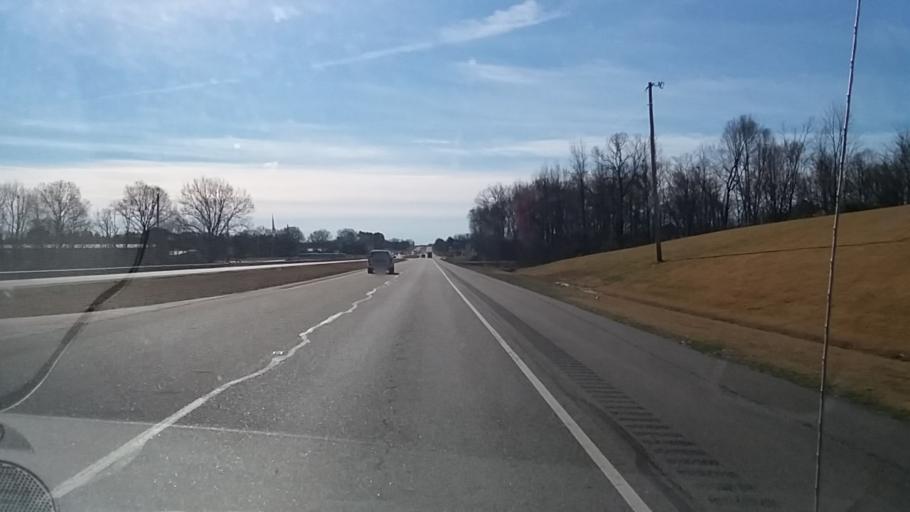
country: US
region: Tennessee
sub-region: Lauderdale County
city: Halls
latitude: 35.9046
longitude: -89.2549
